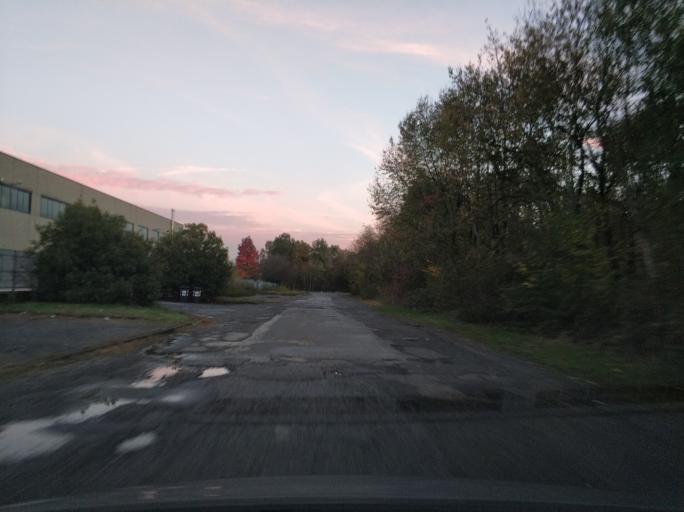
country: IT
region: Piedmont
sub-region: Provincia di Torino
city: Robassomero
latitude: 45.1733
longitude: 7.5923
